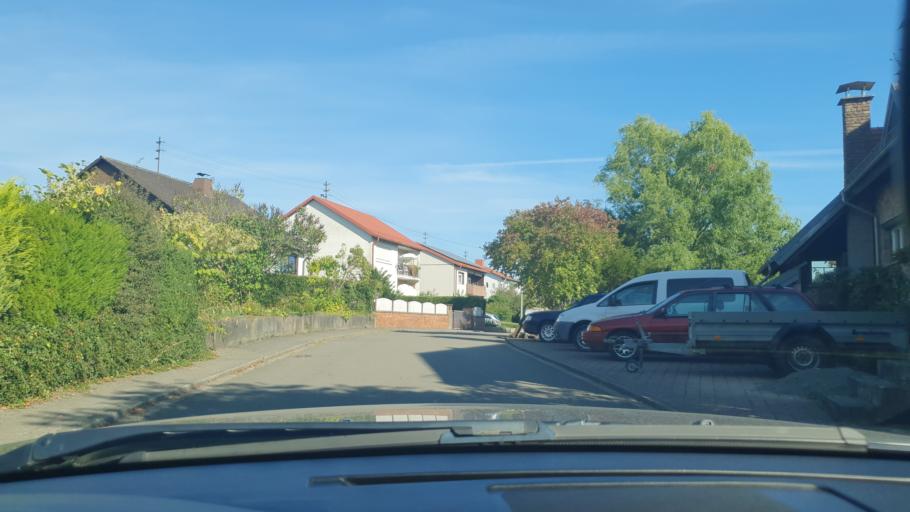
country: DE
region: Rheinland-Pfalz
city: Battweiler
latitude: 49.2793
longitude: 7.4632
